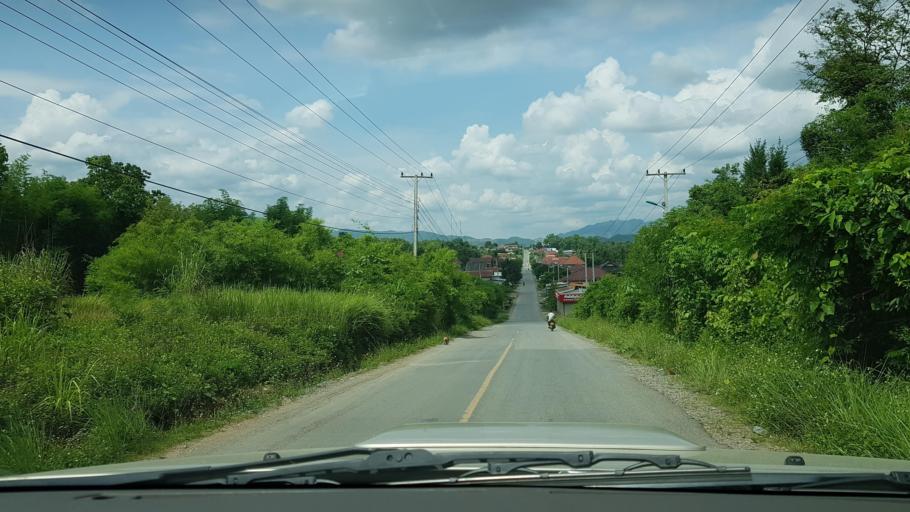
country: LA
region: Loungnamtha
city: Muang Nale
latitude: 20.1319
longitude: 101.4446
